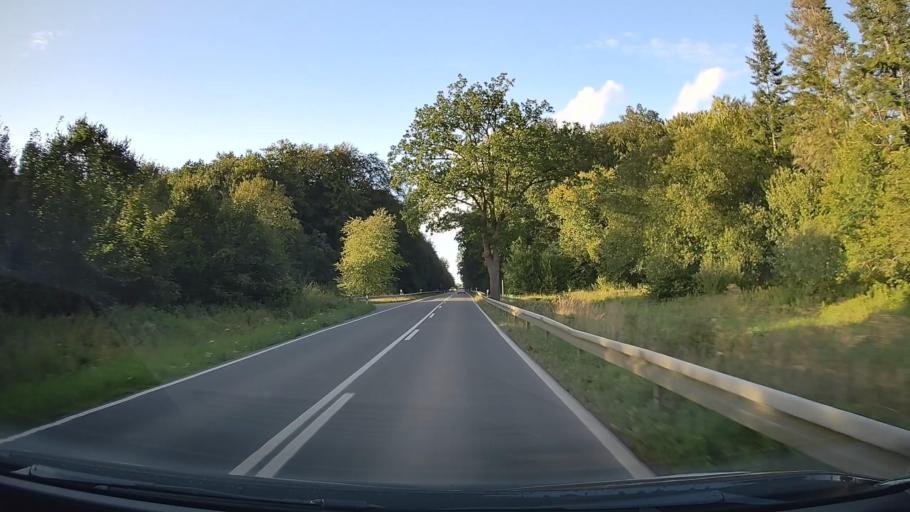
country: DE
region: Mecklenburg-Vorpommern
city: Steinhagen
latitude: 54.2012
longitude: 13.0110
